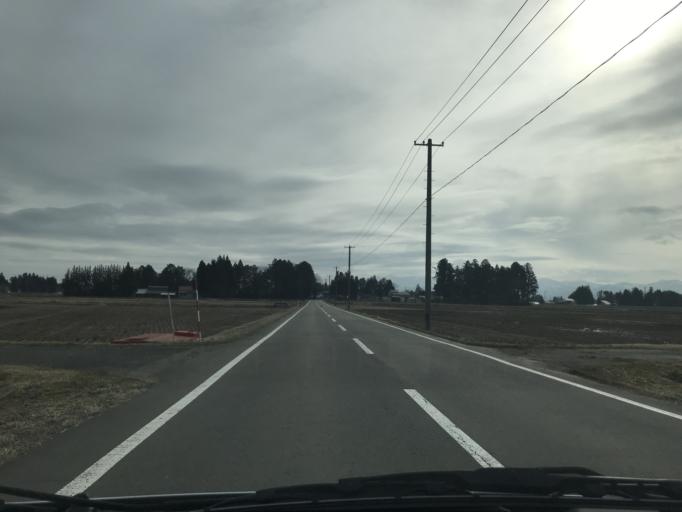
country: JP
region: Iwate
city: Hanamaki
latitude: 39.3579
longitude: 141.0646
